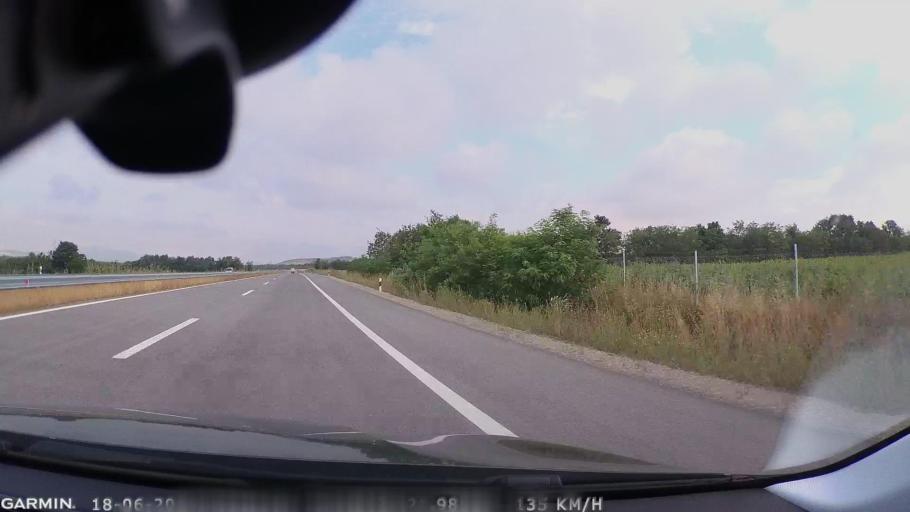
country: MK
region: Sveti Nikole
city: Sveti Nikole
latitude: 41.8377
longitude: 21.9852
